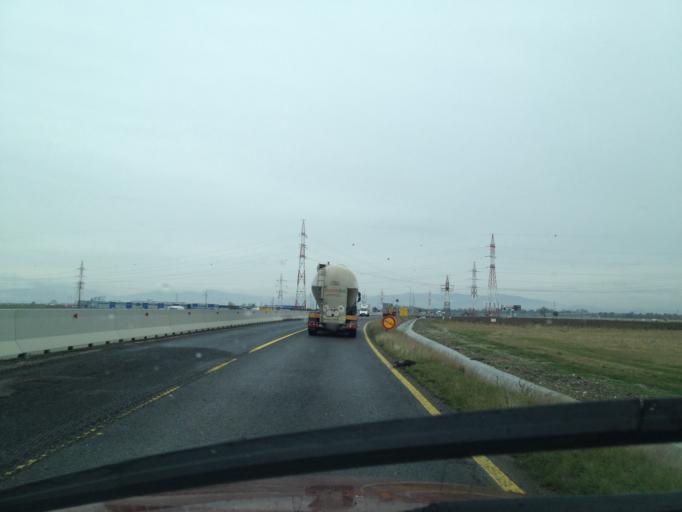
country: RO
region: Brasov
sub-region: Comuna Sanpetru
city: Sanpetru
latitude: 45.6882
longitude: 25.6532
